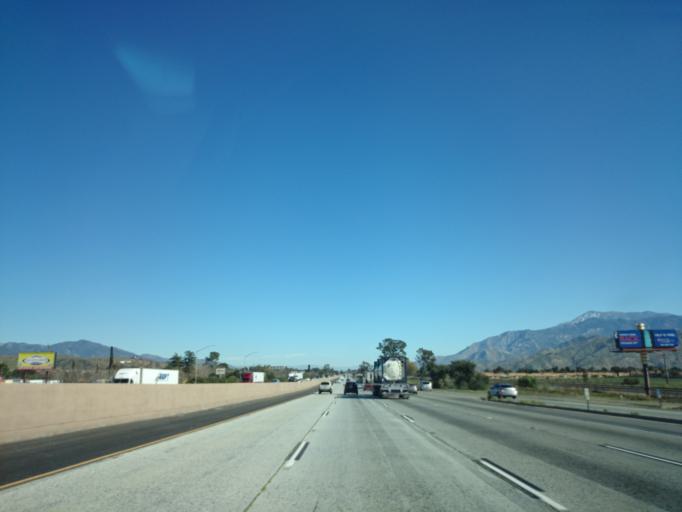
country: US
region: California
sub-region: Riverside County
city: Beaumont
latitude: 33.9267
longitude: -116.9437
